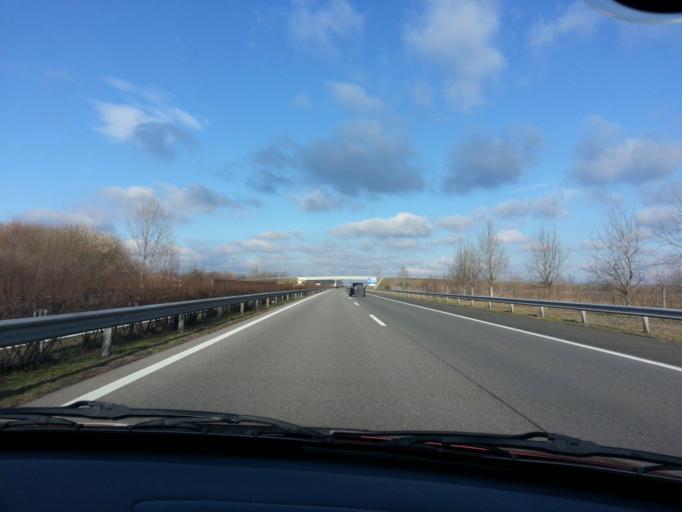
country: HU
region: Csongrad
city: Szatymaz
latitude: 46.3563
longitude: 20.0048
